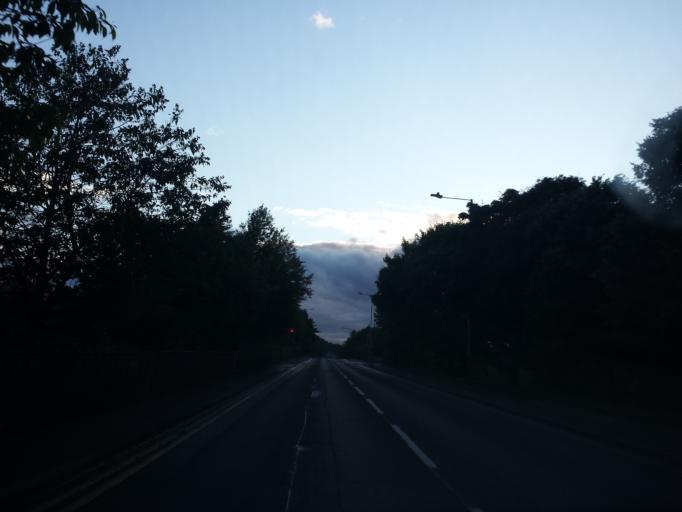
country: GB
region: Scotland
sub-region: Perth and Kinross
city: Perth
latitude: 56.4037
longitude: -3.4454
